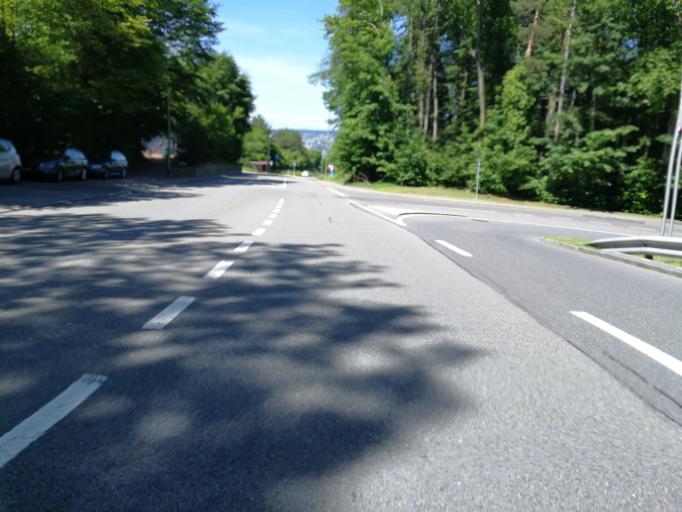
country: CH
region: Zurich
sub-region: Bezirk Horgen
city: Horgen / Allmend
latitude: 47.2489
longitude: 8.6080
